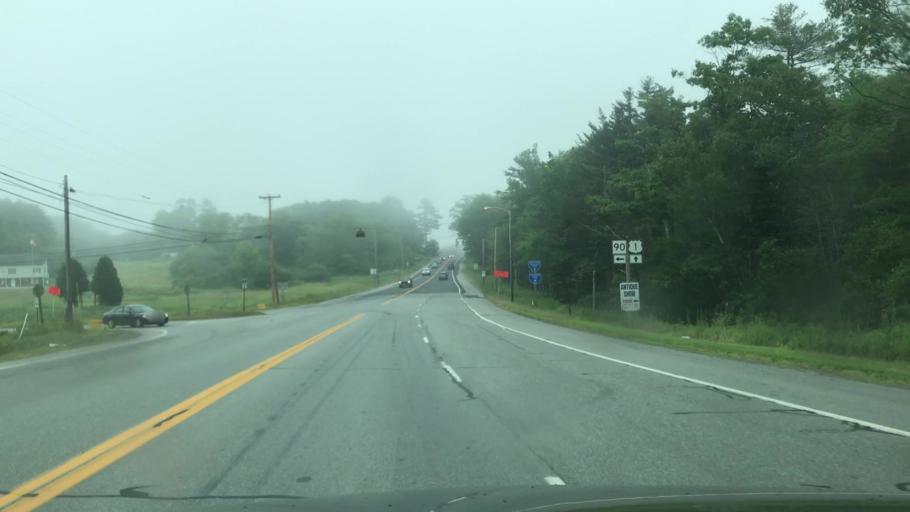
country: US
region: Maine
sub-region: Knox County
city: Warren
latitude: 44.1167
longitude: -69.2640
